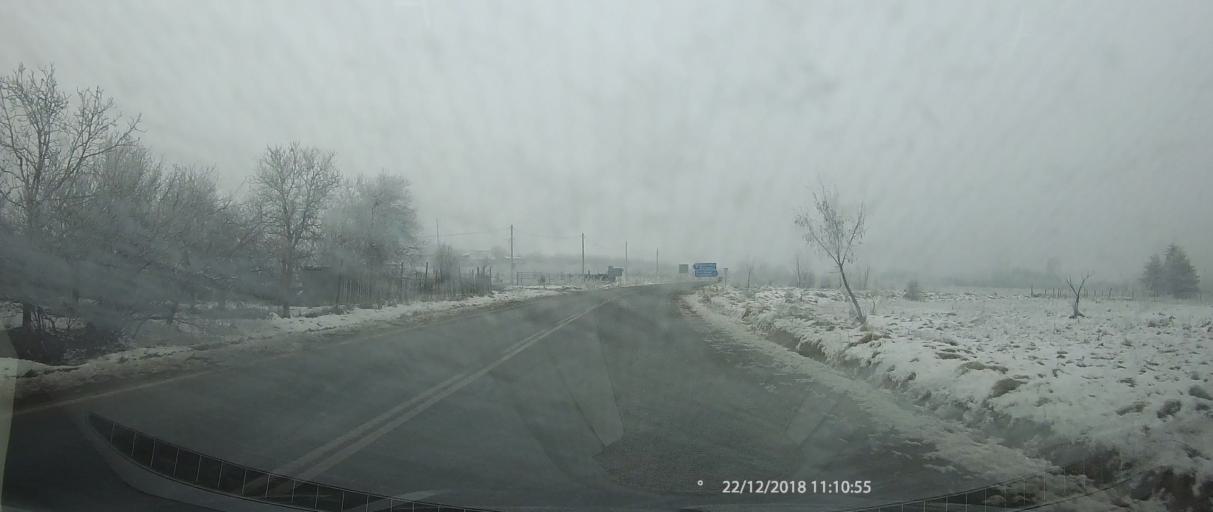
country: BG
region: Kyustendil
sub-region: Obshtina Kyustendil
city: Kyustendil
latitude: 42.2796
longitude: 22.6568
